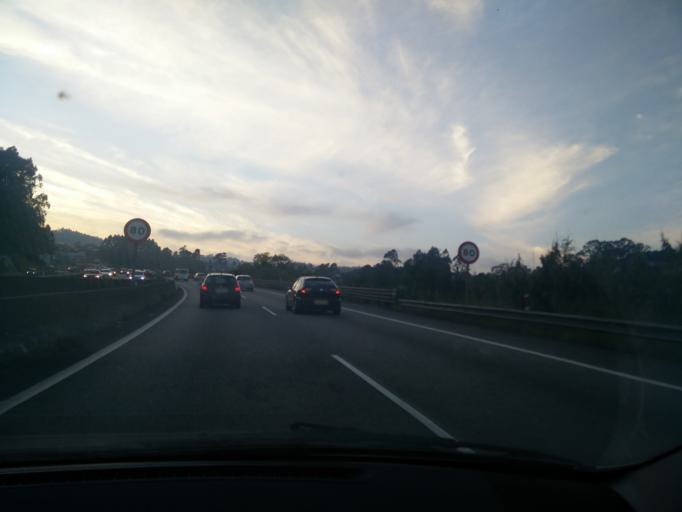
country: ES
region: Galicia
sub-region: Provincia de Pontevedra
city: Porrino
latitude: 42.1918
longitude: -8.6401
